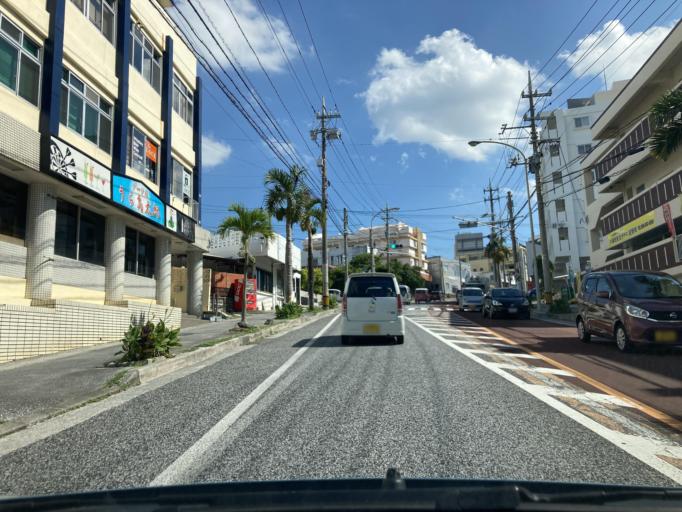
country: JP
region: Okinawa
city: Ginowan
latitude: 26.2653
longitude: 127.7385
